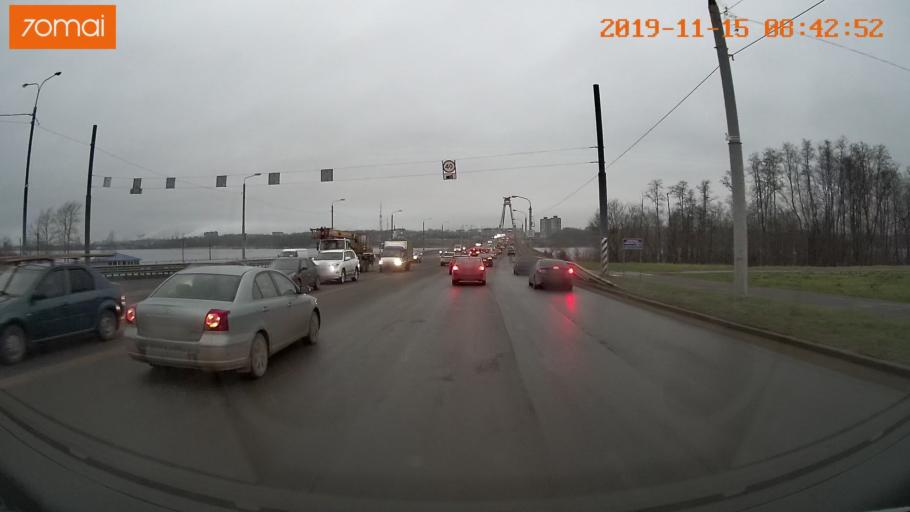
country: RU
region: Vologda
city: Cherepovets
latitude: 59.1064
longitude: 37.9058
